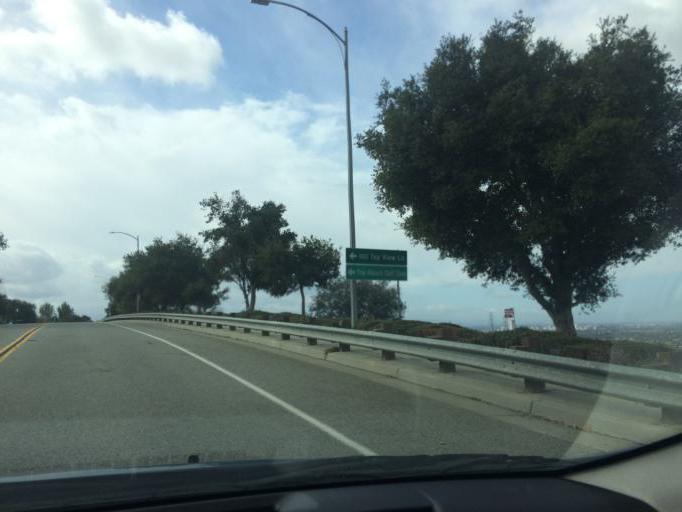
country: US
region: California
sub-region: Santa Clara County
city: Seven Trees
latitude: 37.2889
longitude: -121.7948
